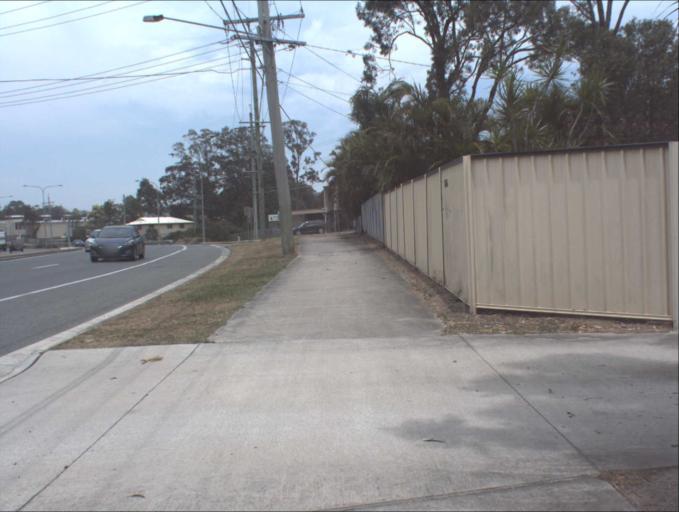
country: AU
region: Queensland
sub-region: Logan
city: Slacks Creek
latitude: -27.6715
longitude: 153.1870
